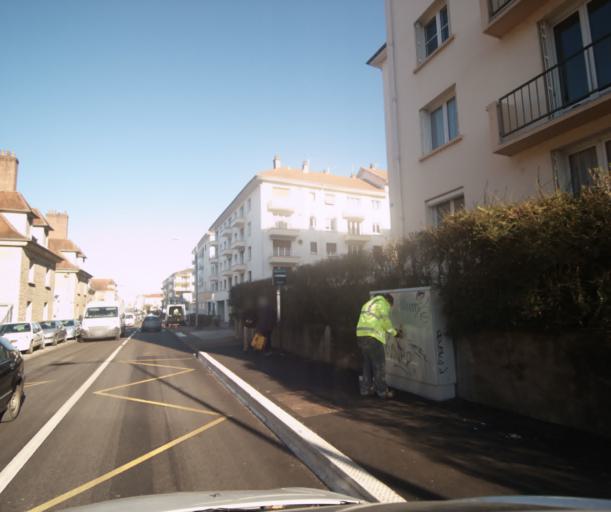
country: FR
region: Franche-Comte
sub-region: Departement du Doubs
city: Besancon
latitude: 47.2348
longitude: 6.0081
